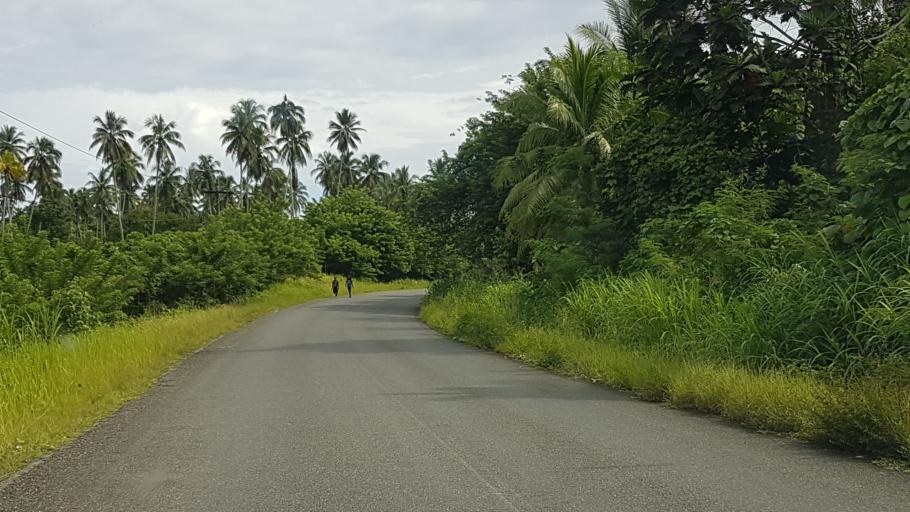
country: PG
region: Madang
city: Madang
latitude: -5.0719
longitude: 145.7728
